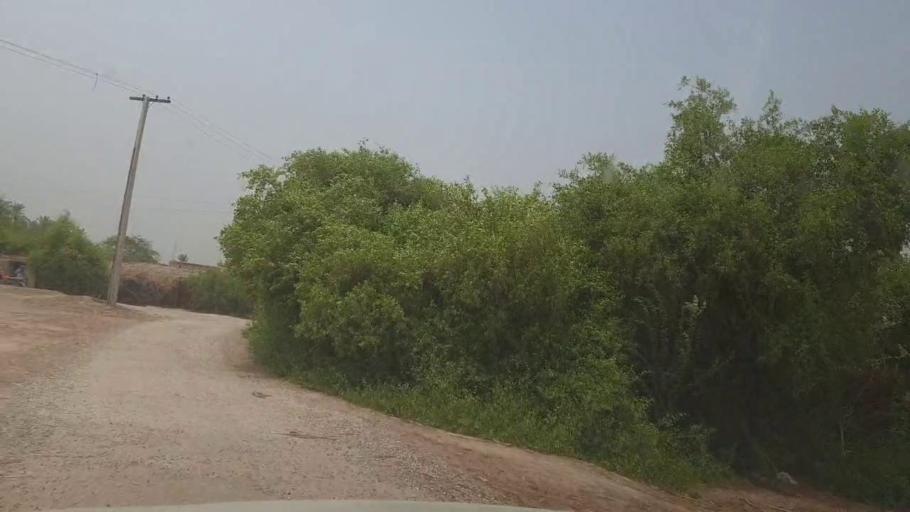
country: PK
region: Sindh
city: Kot Diji
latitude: 27.4410
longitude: 68.6432
